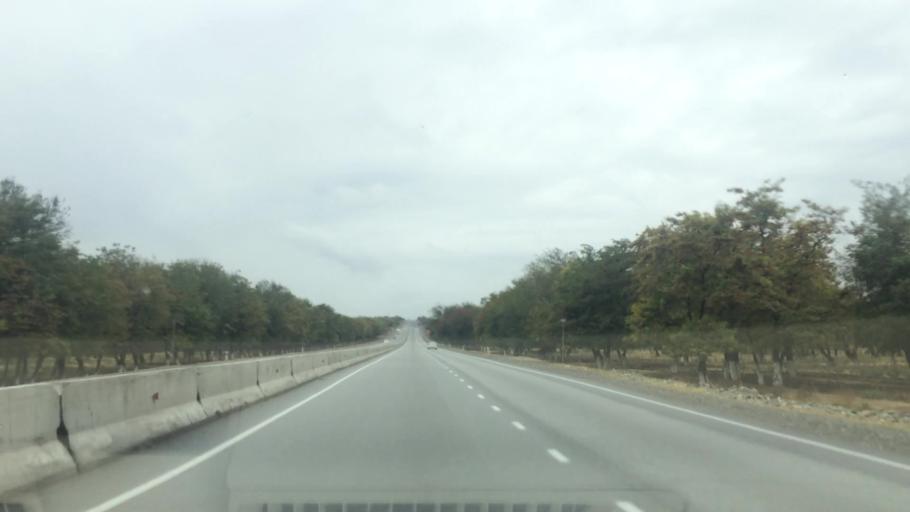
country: UZ
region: Samarqand
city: Bulung'ur
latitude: 39.8718
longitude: 67.4788
